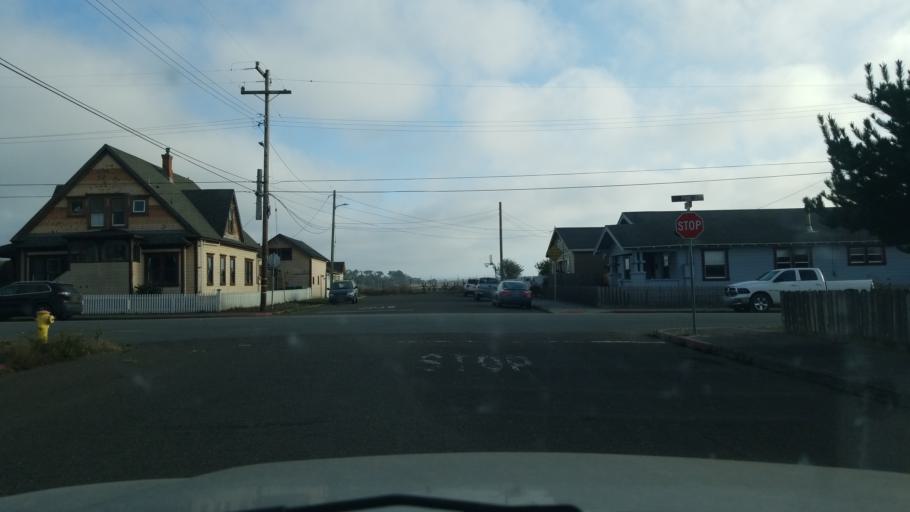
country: US
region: California
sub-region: Mendocino County
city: Fort Bragg
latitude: 39.4470
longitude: -123.8087
